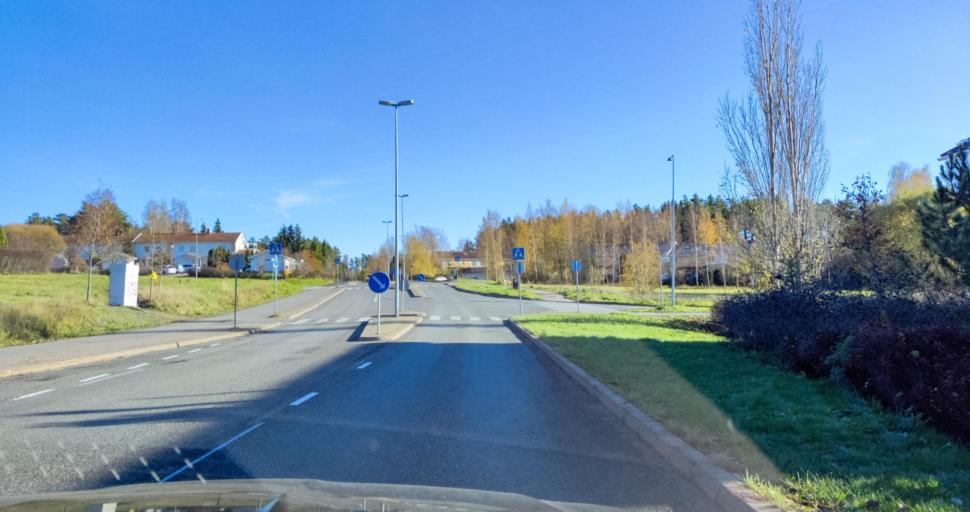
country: FI
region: Varsinais-Suomi
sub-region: Turku
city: Turku
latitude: 60.4090
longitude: 22.2200
